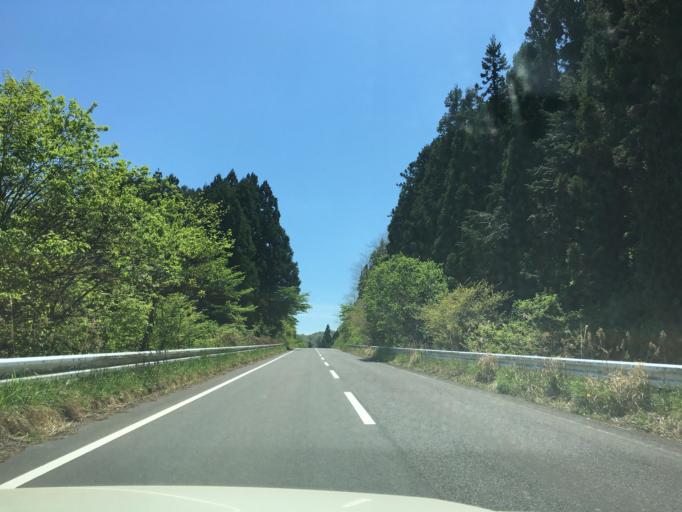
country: JP
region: Fukushima
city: Funehikimachi-funehiki
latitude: 37.3645
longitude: 140.6347
